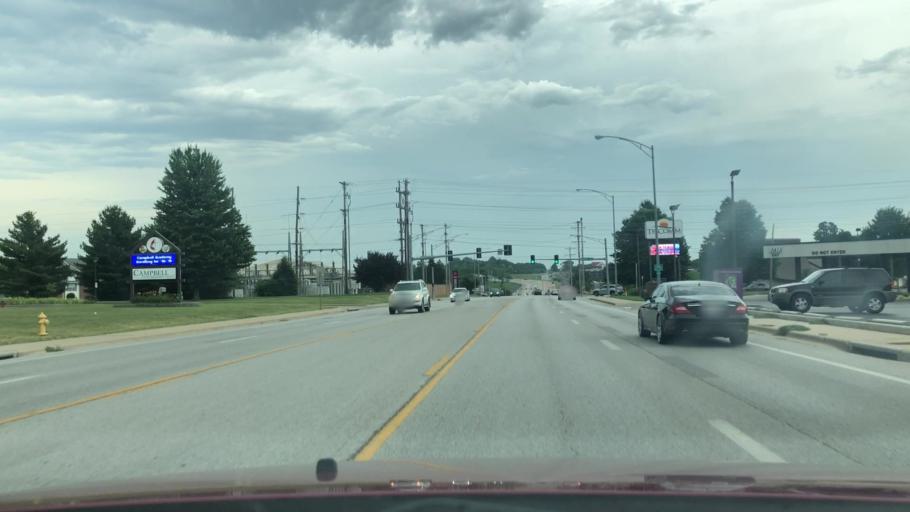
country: US
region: Missouri
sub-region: Greene County
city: Springfield
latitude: 37.1374
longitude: -93.2642
